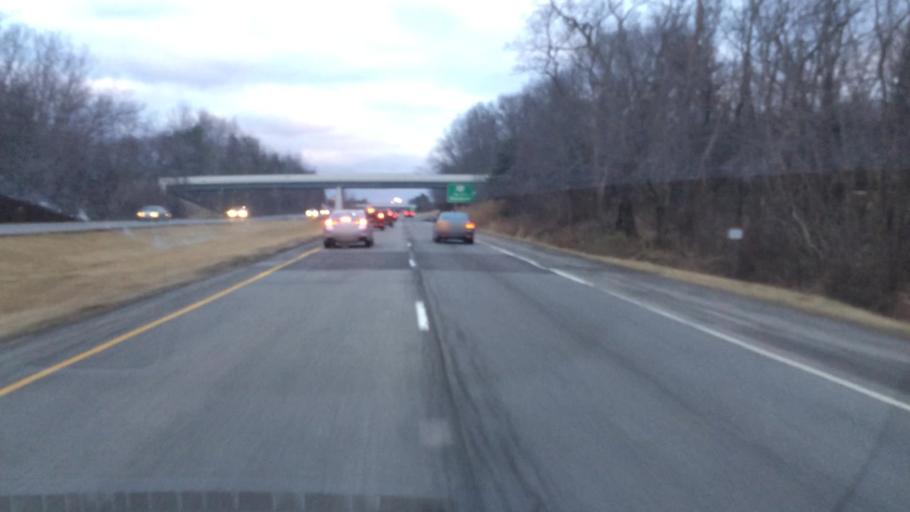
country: US
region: Ohio
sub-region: Summit County
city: Norton
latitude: 41.0563
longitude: -81.6624
